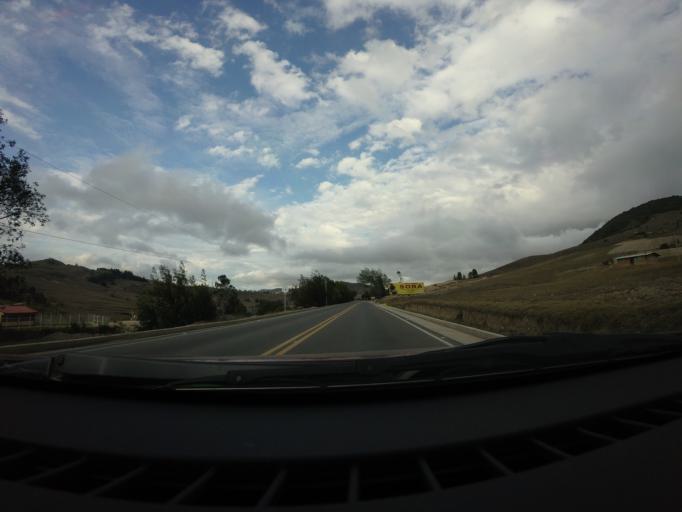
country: CO
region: Boyaca
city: Cucaita
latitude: 5.5655
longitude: -73.4268
